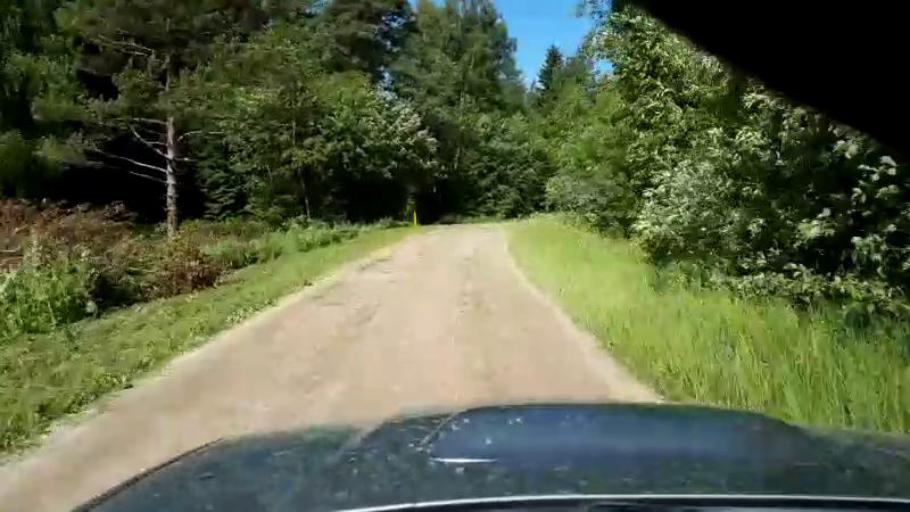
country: EE
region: Paernumaa
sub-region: Sindi linn
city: Sindi
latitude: 58.5198
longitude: 24.6498
